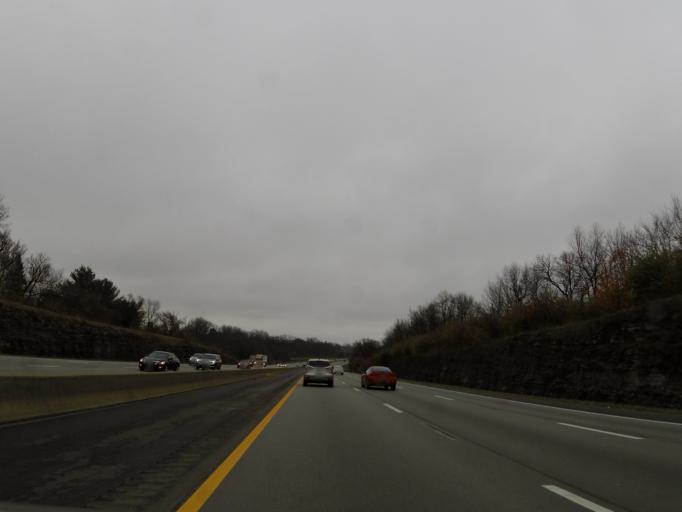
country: US
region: Kentucky
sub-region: Scott County
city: Georgetown
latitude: 38.1992
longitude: -84.5270
